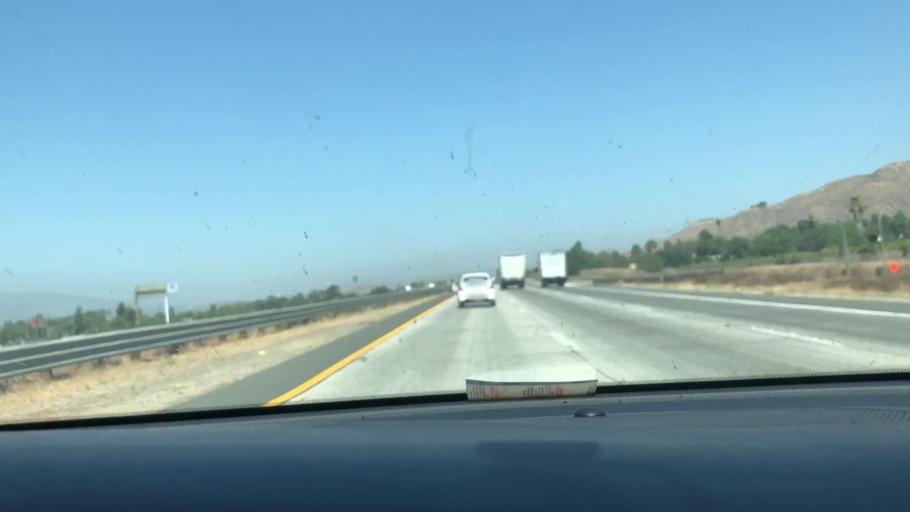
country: US
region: California
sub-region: Riverside County
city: Sedco Hills
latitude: 33.6258
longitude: -117.2719
